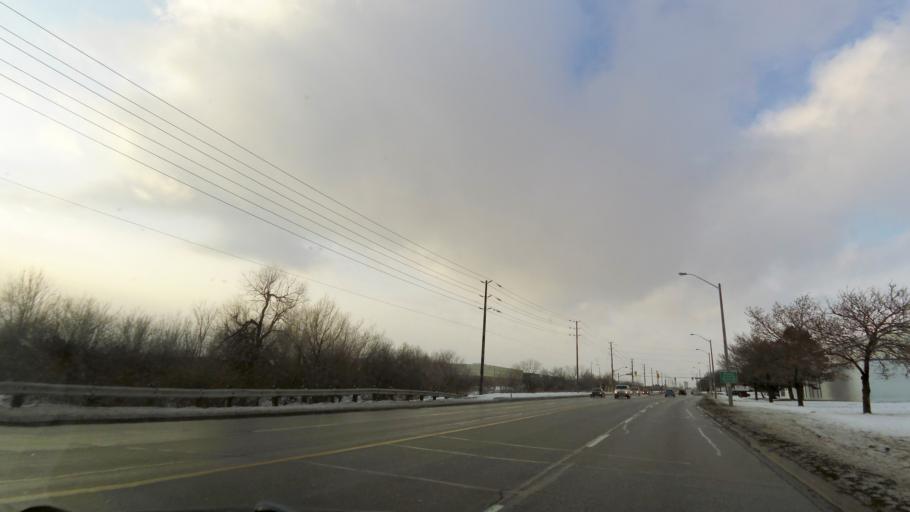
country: CA
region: Ontario
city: Brampton
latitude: 43.6849
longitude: -79.6993
